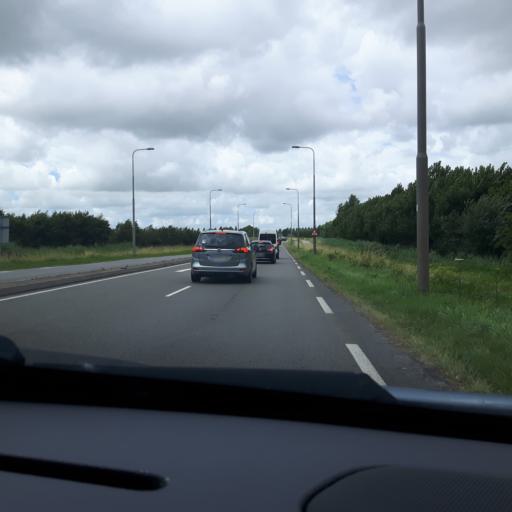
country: NL
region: Zeeland
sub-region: Gemeente Goes
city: Goes
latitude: 51.5068
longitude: 3.8709
